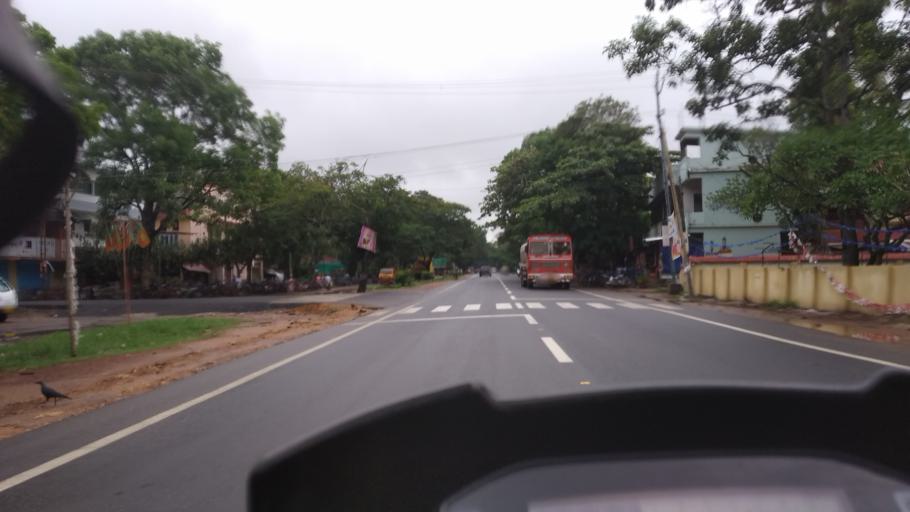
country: IN
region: Kerala
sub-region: Alappuzha
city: Mavelikara
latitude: 9.3029
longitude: 76.4327
